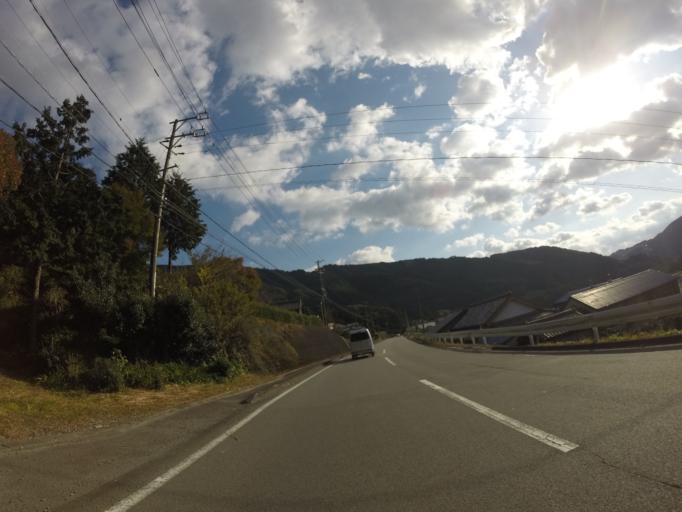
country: JP
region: Shizuoka
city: Kanaya
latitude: 34.8924
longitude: 138.1186
